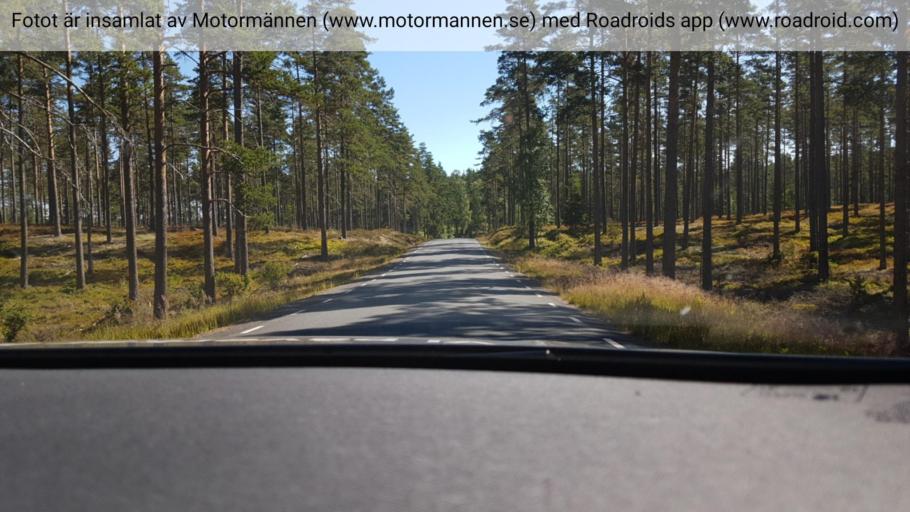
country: SE
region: Vaestra Goetaland
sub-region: Tidaholms Kommun
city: Tidaholm
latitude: 58.1025
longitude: 14.1020
